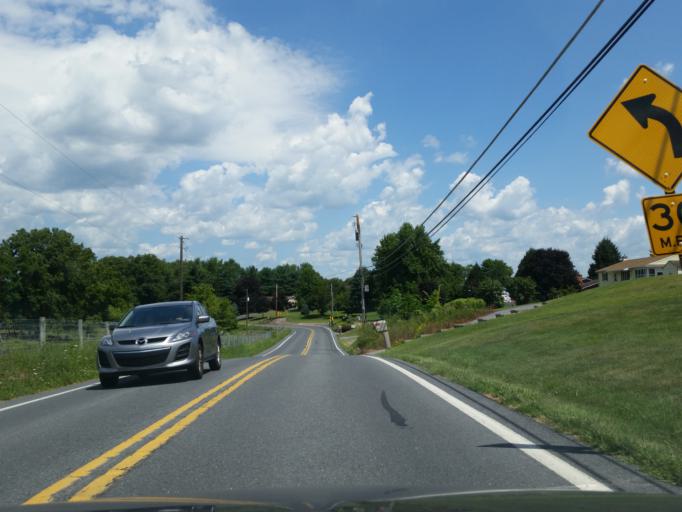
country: US
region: Pennsylvania
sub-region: Lebanon County
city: Annville
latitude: 40.3594
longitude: -76.5134
